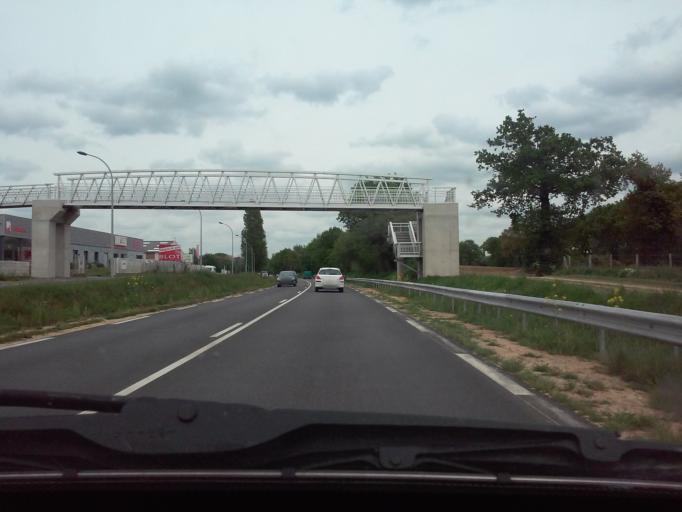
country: FR
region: Brittany
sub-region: Departement d'Ille-et-Vilaine
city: Montgermont
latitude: 48.1503
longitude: -1.7158
